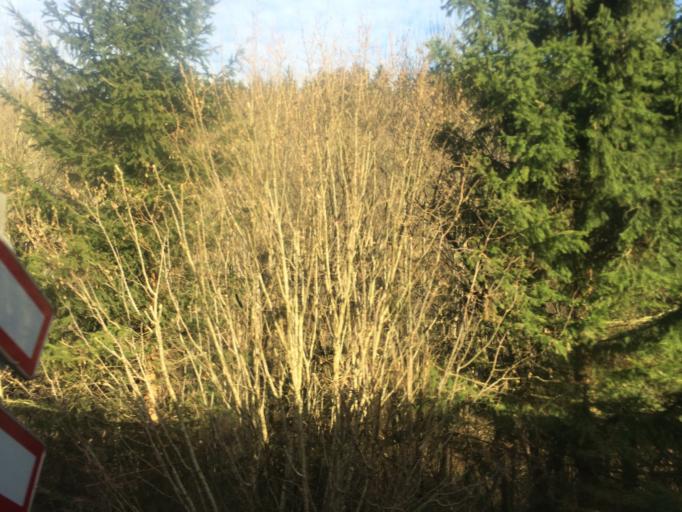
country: DK
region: South Denmark
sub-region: Vejle Kommune
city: Vejle
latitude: 55.7598
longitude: 9.4982
